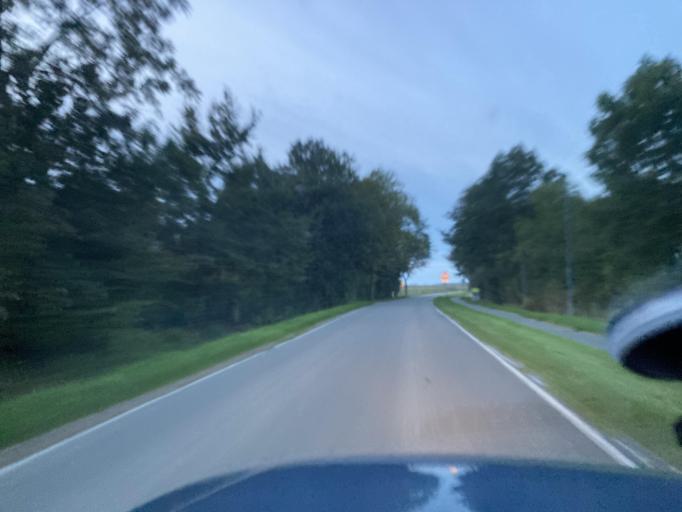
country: DE
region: Schleswig-Holstein
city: Welt
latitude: 54.3037
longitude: 8.7913
